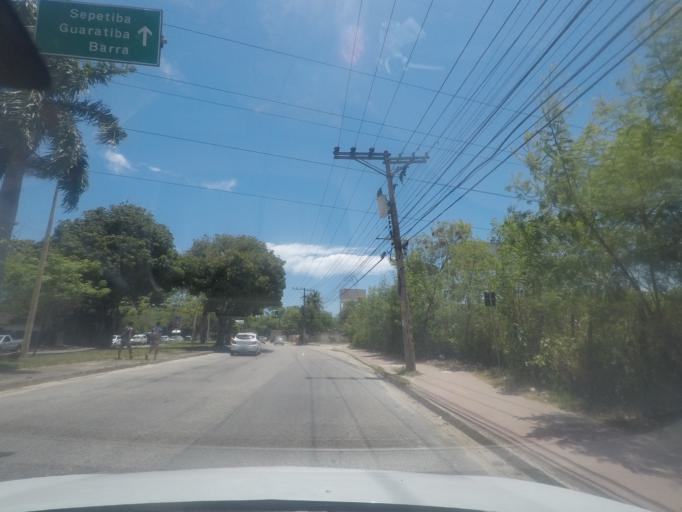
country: BR
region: Rio de Janeiro
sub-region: Itaguai
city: Itaguai
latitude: -22.9018
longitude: -43.6813
